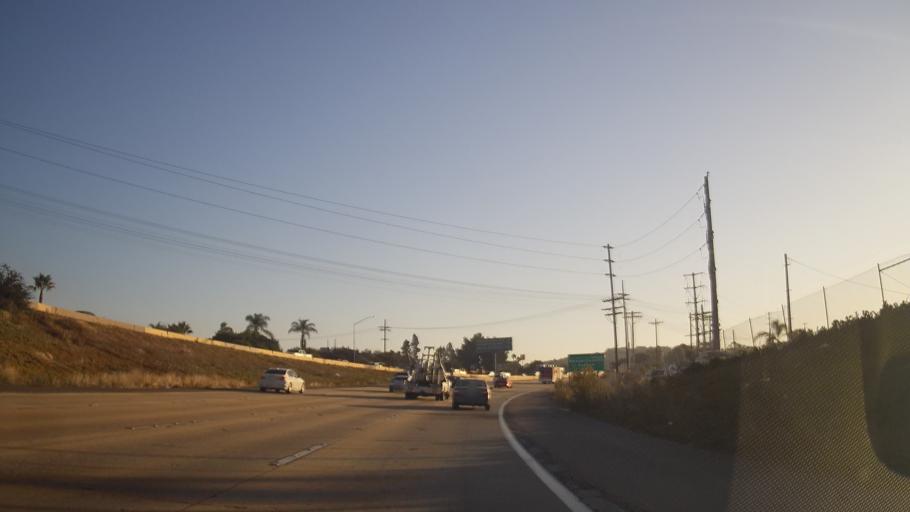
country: US
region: California
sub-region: San Diego County
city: Lemon Grove
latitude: 32.7438
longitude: -117.0478
